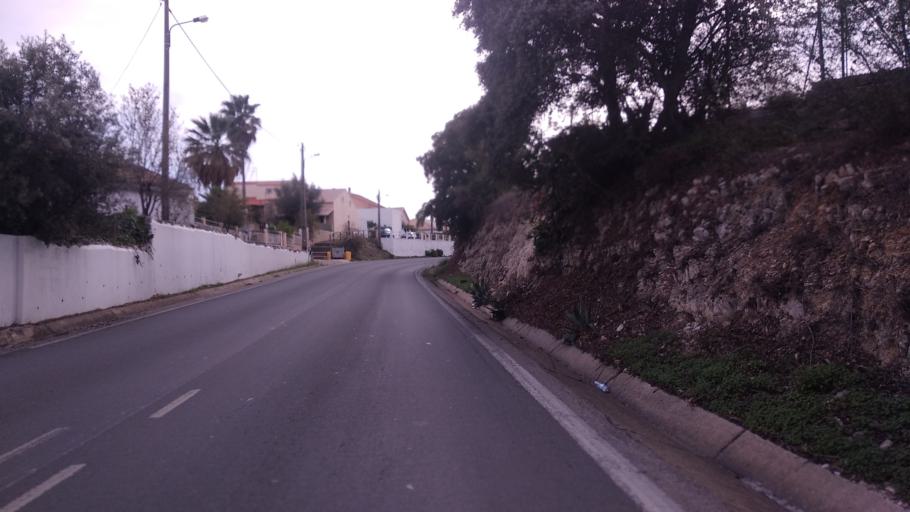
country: PT
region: Faro
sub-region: Loule
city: Loule
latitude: 37.1436
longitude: -7.9809
